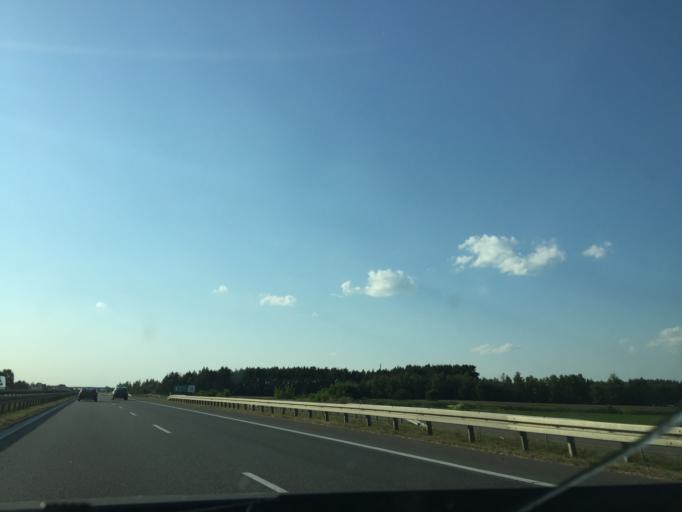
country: PL
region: Masovian Voivodeship
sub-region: Powiat radomski
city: Jedlinsk
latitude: 51.5394
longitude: 21.0664
